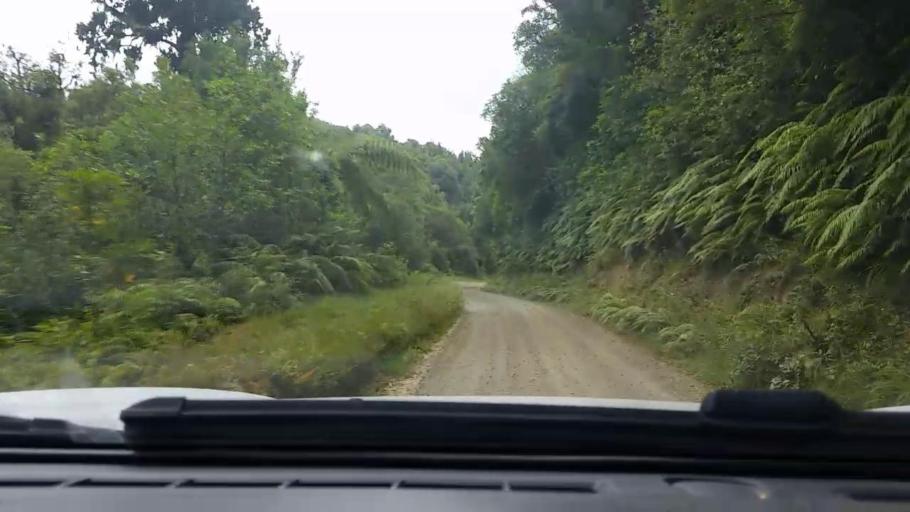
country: NZ
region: Bay of Plenty
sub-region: Kawerau District
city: Kawerau
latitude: -38.0043
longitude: 176.5973
